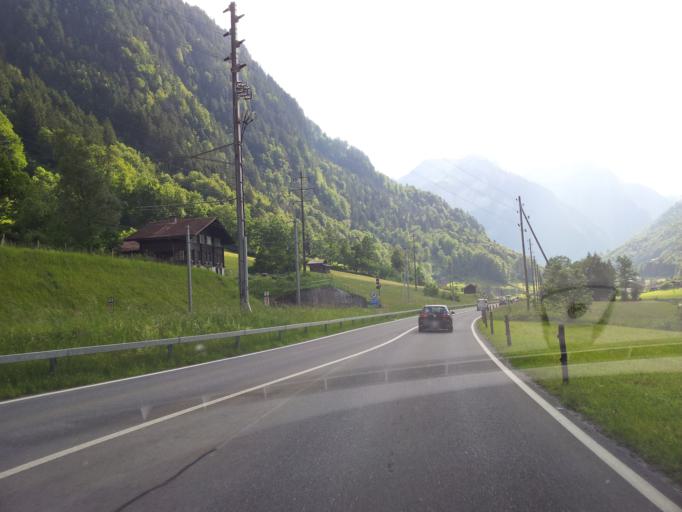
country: CH
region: Bern
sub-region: Interlaken-Oberhasli District
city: Lauterbrunnen
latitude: 46.6372
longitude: 7.9480
